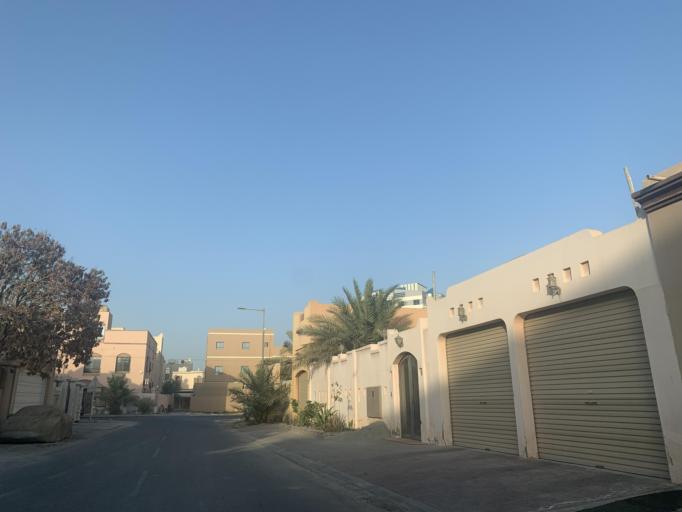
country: BH
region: Manama
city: Jidd Hafs
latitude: 26.1993
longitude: 50.5308
